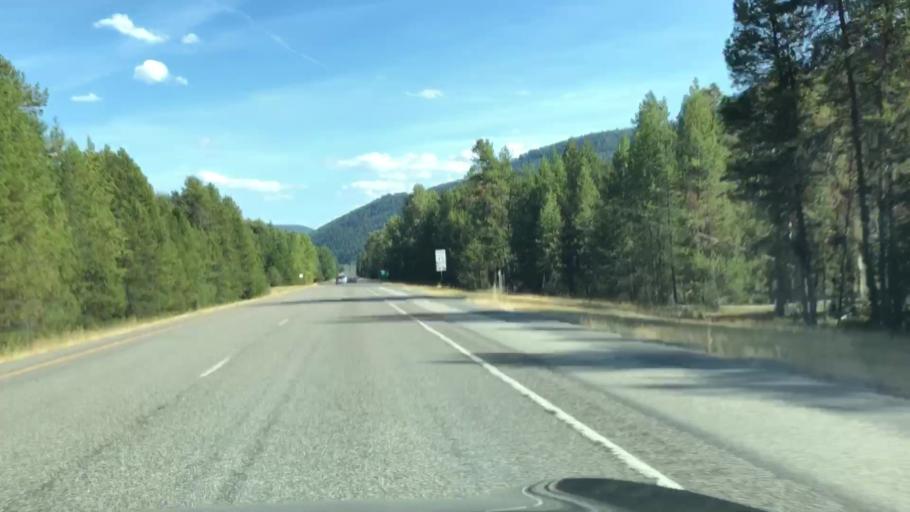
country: US
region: Montana
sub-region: Sanders County
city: Thompson Falls
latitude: 47.3706
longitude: -115.3395
